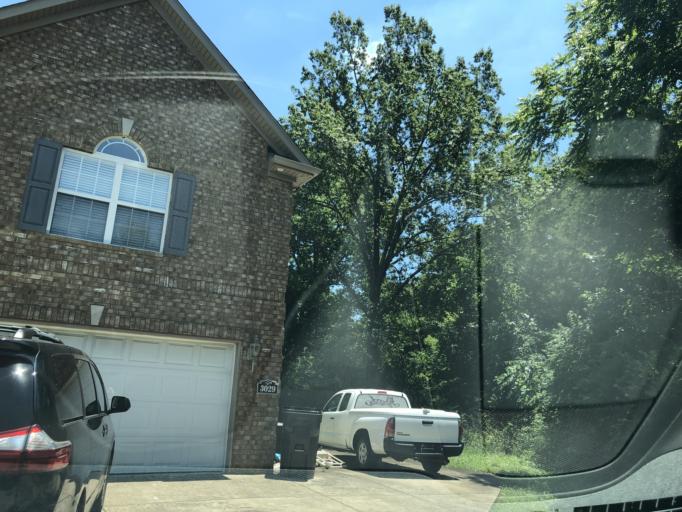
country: US
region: Tennessee
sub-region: Williamson County
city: Nolensville
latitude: 36.0186
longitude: -86.6556
